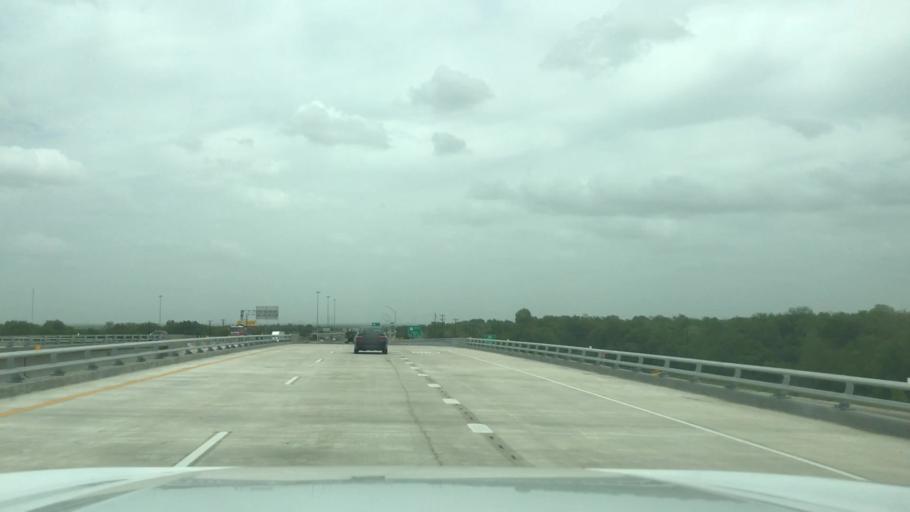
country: US
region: Texas
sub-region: McLennan County
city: Beverly
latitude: 31.4945
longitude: -97.1336
